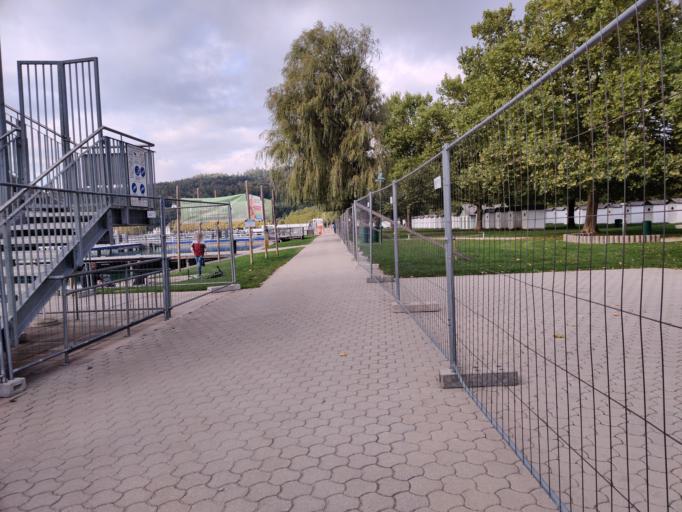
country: AT
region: Carinthia
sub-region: Klagenfurt am Woerthersee
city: Klagenfurt am Woerthersee
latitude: 46.6175
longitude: 14.2546
